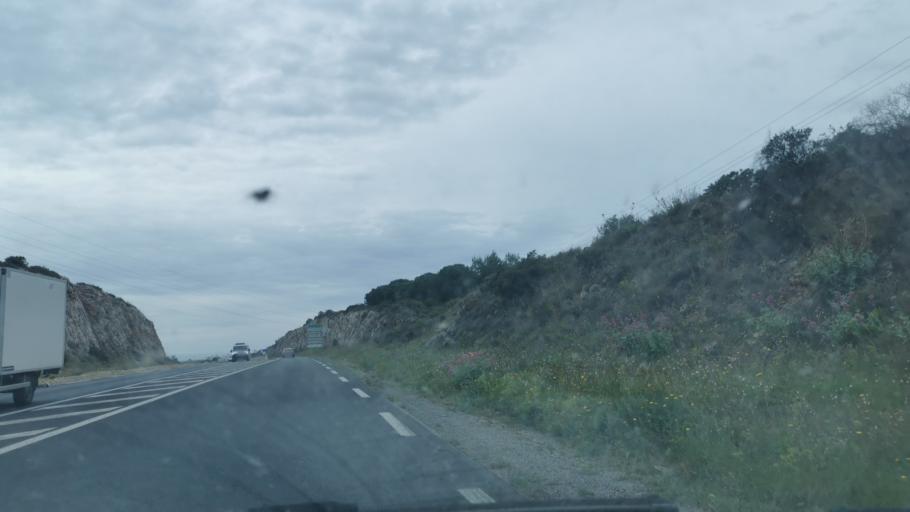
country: FR
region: Languedoc-Roussillon
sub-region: Departement de l'Herault
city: Balaruc-le-Vieux
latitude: 43.4517
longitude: 3.7058
